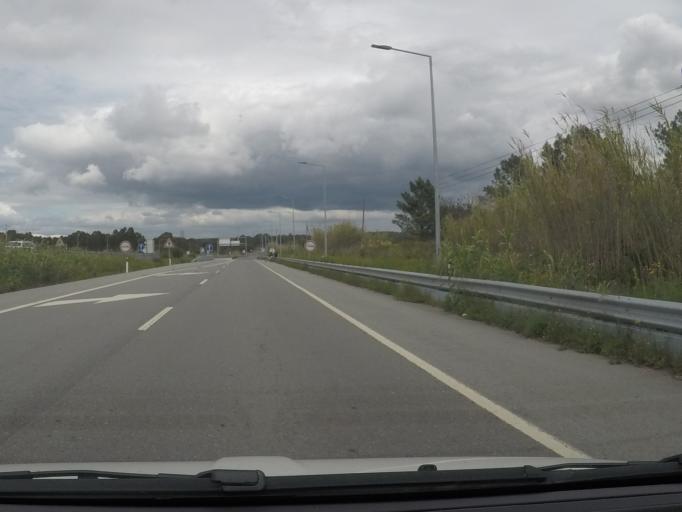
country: PT
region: Setubal
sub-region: Sines
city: Sines
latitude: 37.9698
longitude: -8.8277
